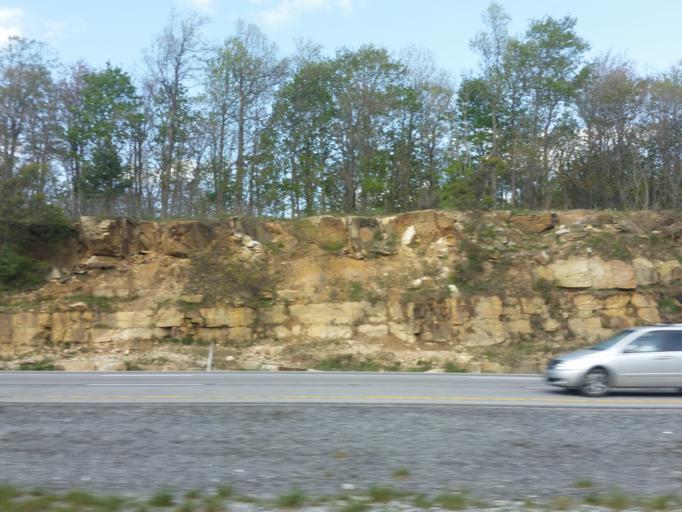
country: US
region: West Virginia
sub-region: Raleigh County
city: Shady Spring
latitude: 37.5788
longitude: -81.1166
